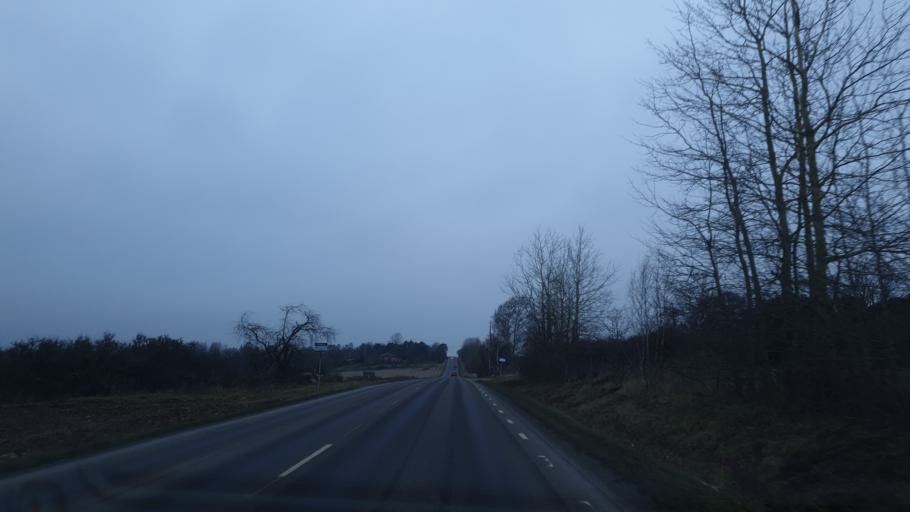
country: SE
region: Blekinge
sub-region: Karlskrona Kommun
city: Jaemjoe
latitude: 56.1454
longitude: 15.7577
